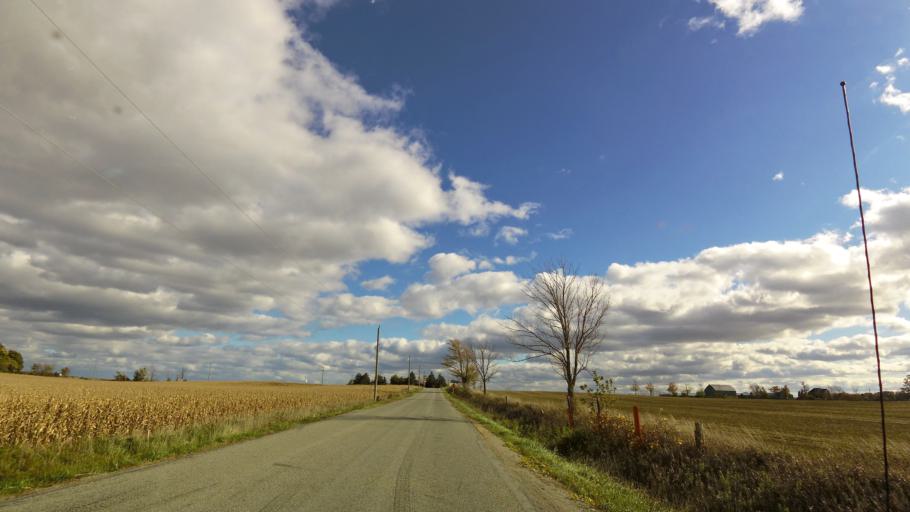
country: CA
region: Ontario
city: Burlington
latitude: 43.4344
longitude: -79.8317
